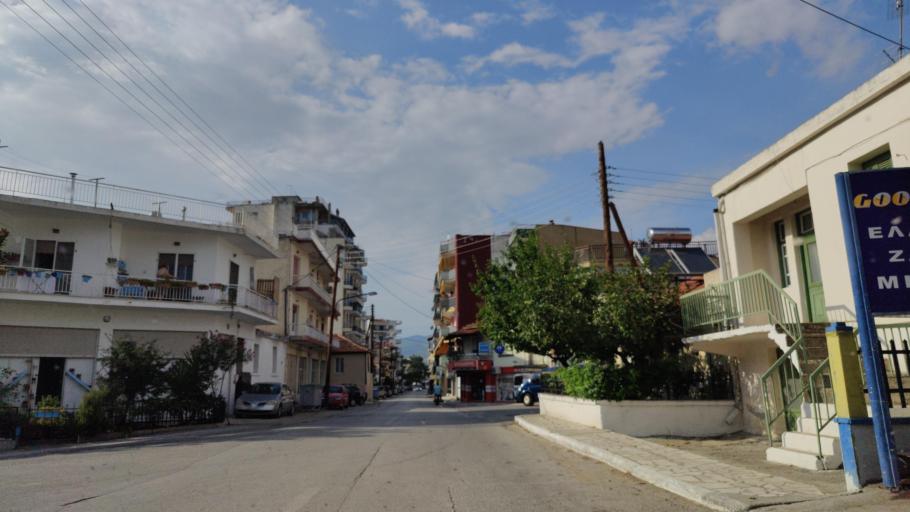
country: GR
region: Central Macedonia
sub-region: Nomos Serron
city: Sidirokastro
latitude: 41.2324
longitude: 23.3905
